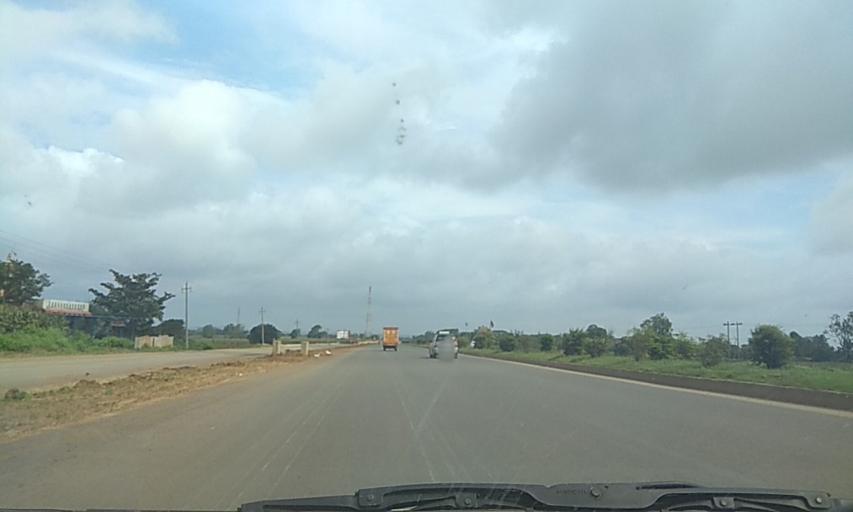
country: IN
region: Karnataka
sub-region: Dharwad
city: Kundgol
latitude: 15.1790
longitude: 75.1390
